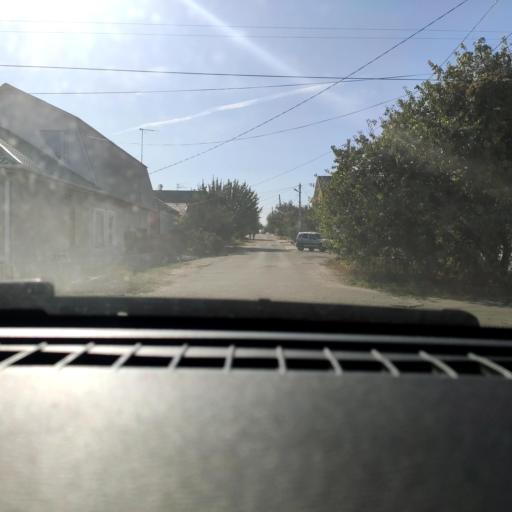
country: RU
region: Voronezj
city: Voronezh
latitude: 51.6720
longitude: 39.2671
